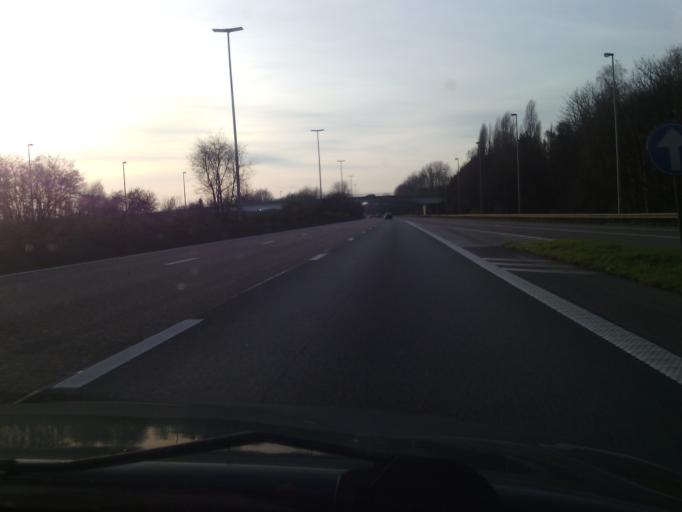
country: BE
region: Flanders
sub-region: Provincie Oost-Vlaanderen
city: Destelbergen
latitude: 51.0490
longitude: 3.8130
